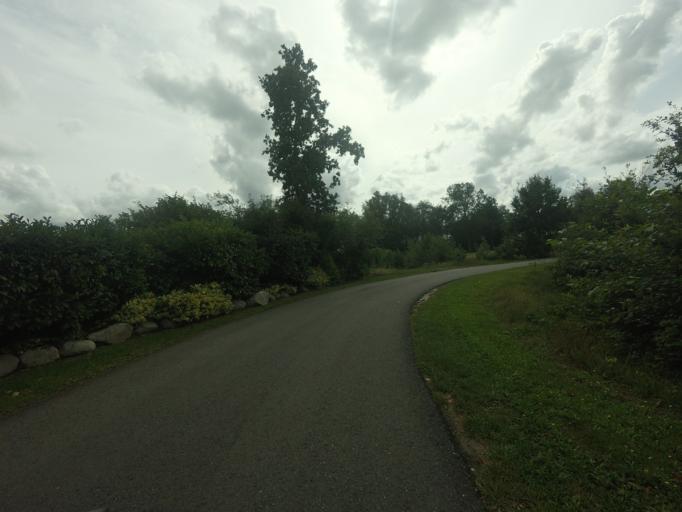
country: NL
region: Drenthe
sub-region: Gemeente Westerveld
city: Dwingeloo
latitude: 52.9635
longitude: 6.3507
